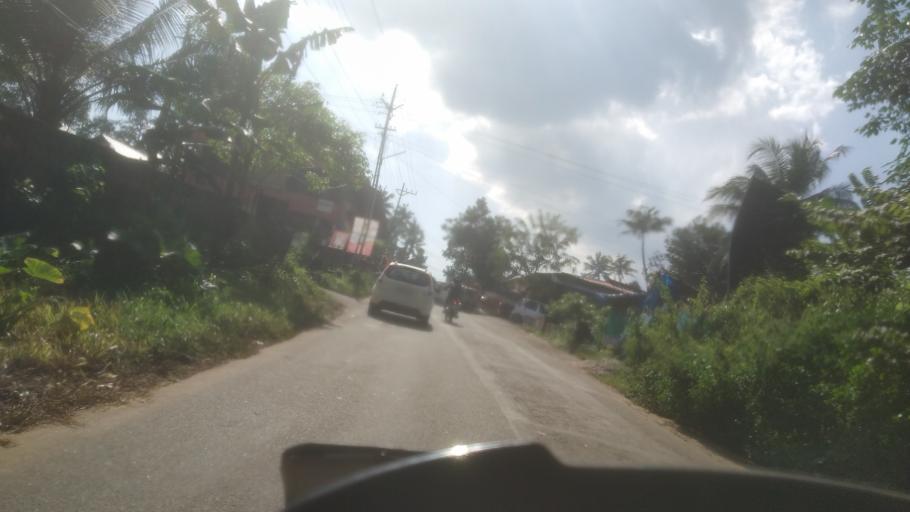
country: IN
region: Kerala
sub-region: Ernakulam
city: Kotamangalam
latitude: 10.0047
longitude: 76.6873
